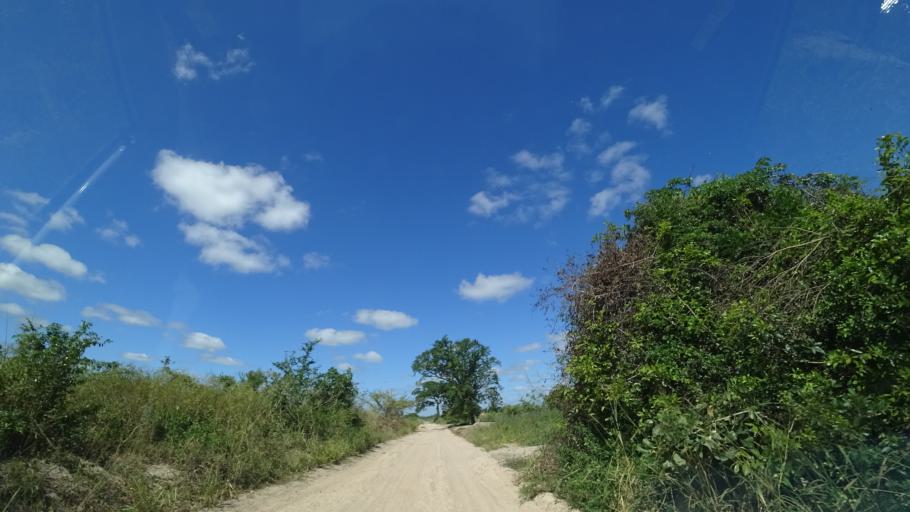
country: MZ
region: Sofala
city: Dondo
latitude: -19.2898
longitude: 34.6885
